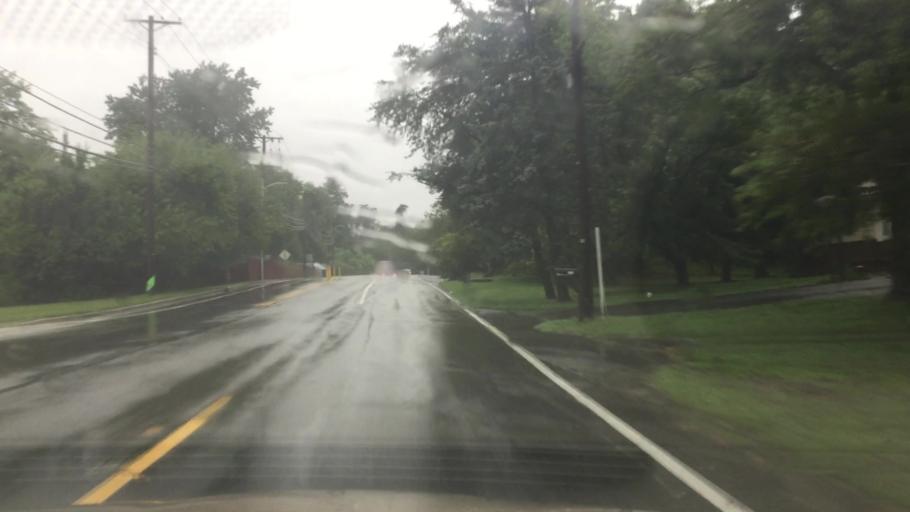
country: US
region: Maryland
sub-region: Anne Arundel County
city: Severn
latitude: 39.1411
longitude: -76.7259
